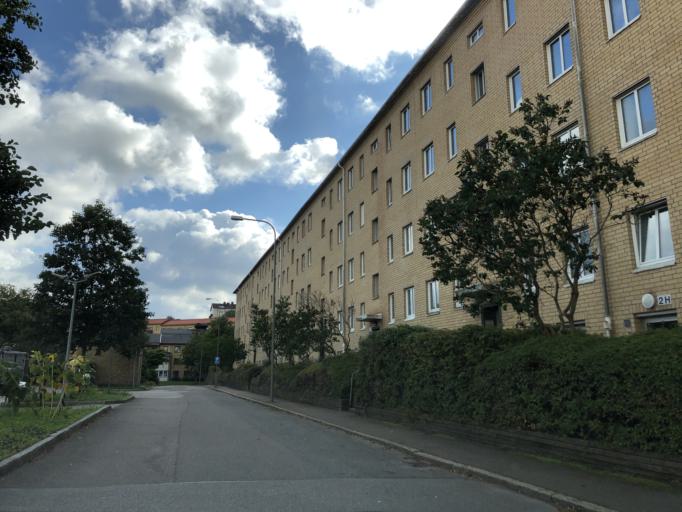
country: SE
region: Vaestra Goetaland
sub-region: Goteborg
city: Goeteborg
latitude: 57.7218
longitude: 12.0143
